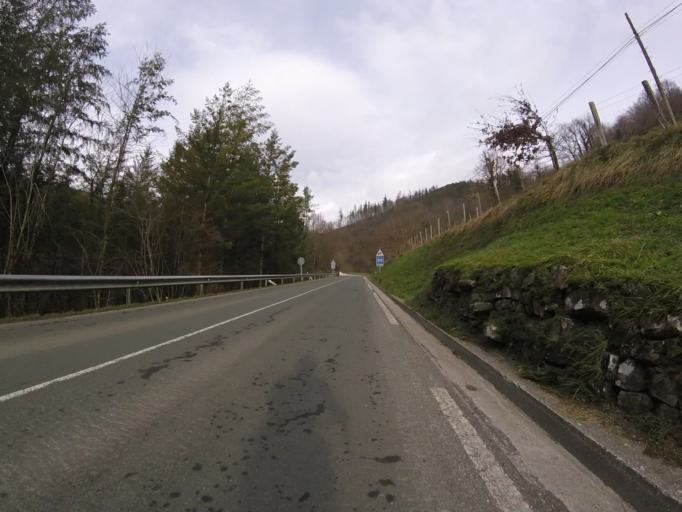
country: ES
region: Basque Country
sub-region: Provincia de Guipuzcoa
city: Albiztur
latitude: 43.1235
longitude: -2.1544
